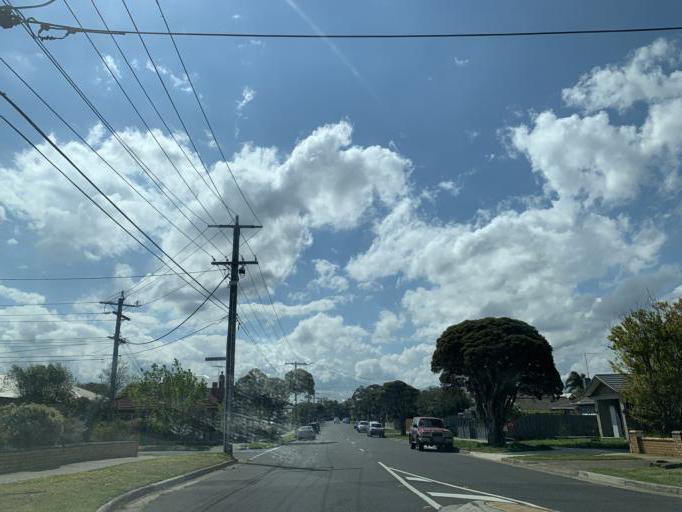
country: AU
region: Victoria
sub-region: Kingston
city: Mordialloc
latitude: -38.0011
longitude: 145.0873
